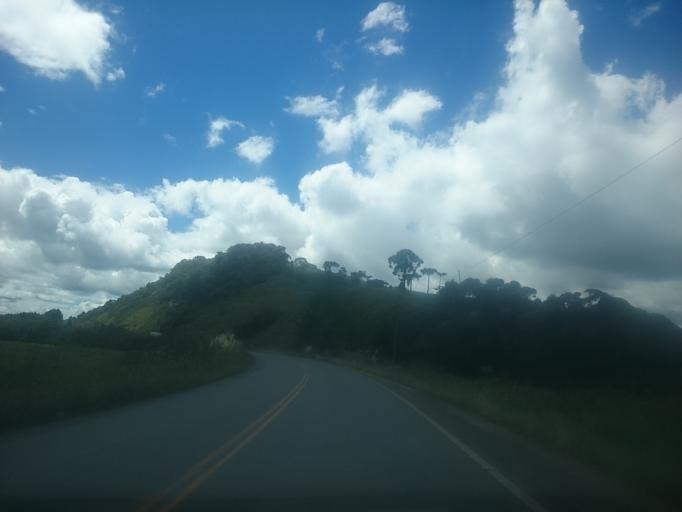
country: BR
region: Santa Catarina
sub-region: Otacilio Costa
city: Otacilio Costa
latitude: -27.6522
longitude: -50.1905
